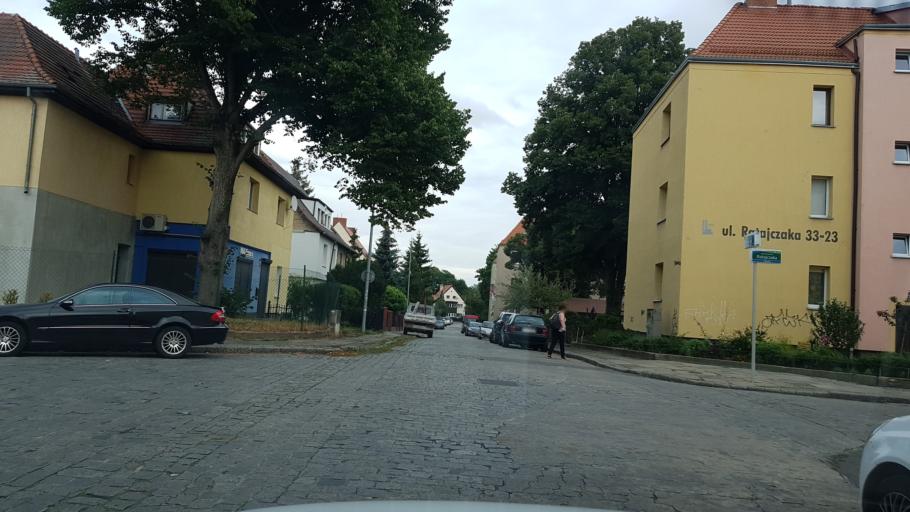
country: PL
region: West Pomeranian Voivodeship
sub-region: Szczecin
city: Szczecin
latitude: 53.4360
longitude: 14.5040
